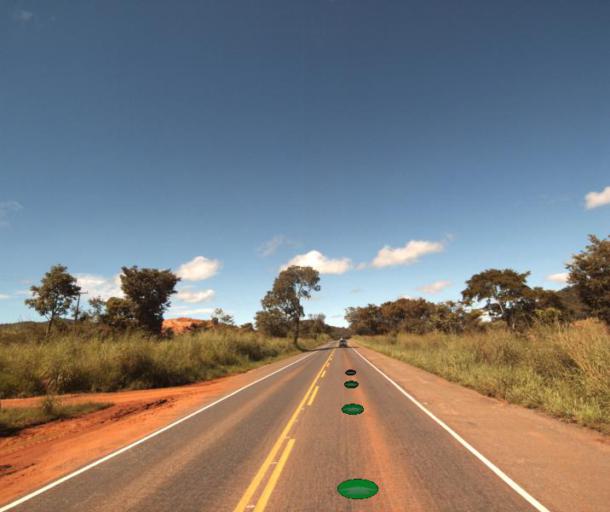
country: BR
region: Goias
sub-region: Rialma
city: Rialma
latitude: -15.2625
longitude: -49.5472
